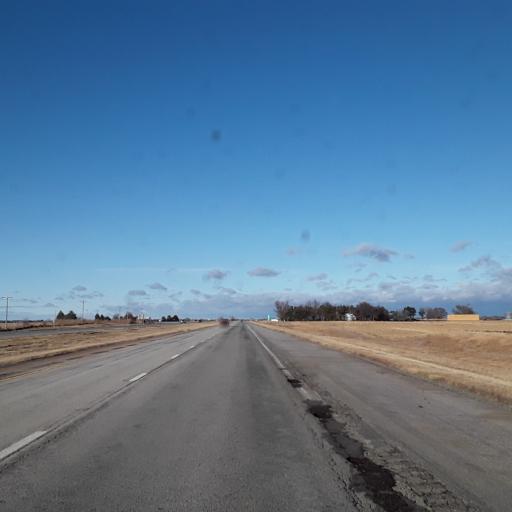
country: US
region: Kansas
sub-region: Republic County
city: Belleville
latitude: 39.7922
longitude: -97.6517
